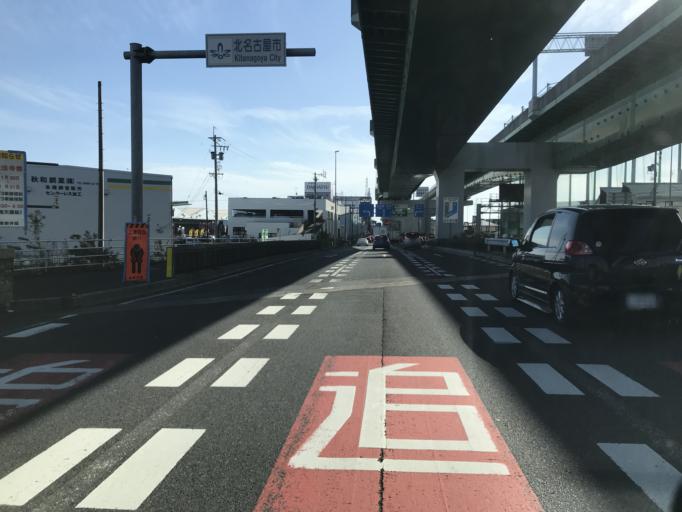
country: JP
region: Aichi
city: Iwakura
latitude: 35.2587
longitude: 136.8423
